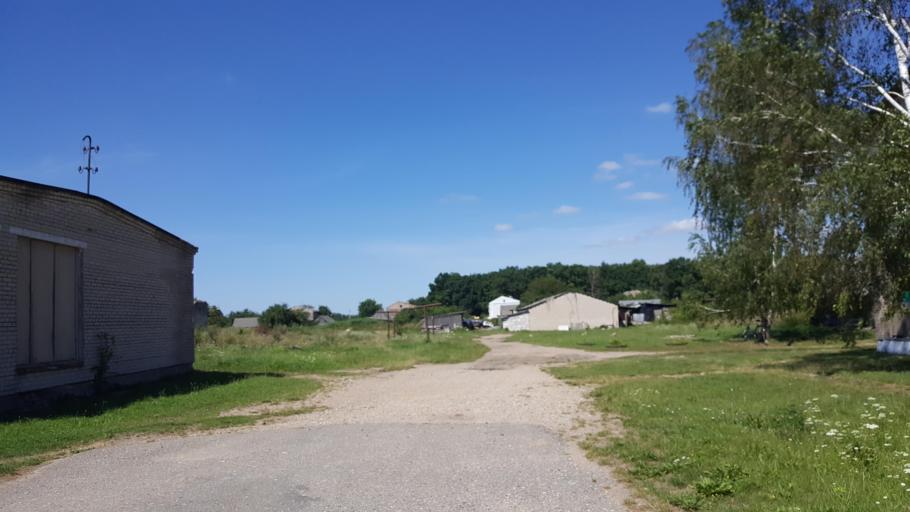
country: BY
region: Brest
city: Kamyanyets
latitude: 52.3681
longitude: 23.6265
